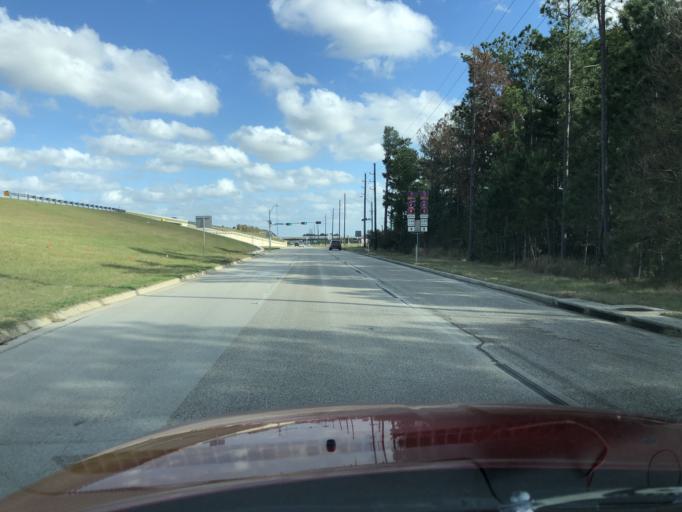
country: US
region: Texas
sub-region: Harris County
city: Tomball
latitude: 30.0514
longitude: -95.6220
